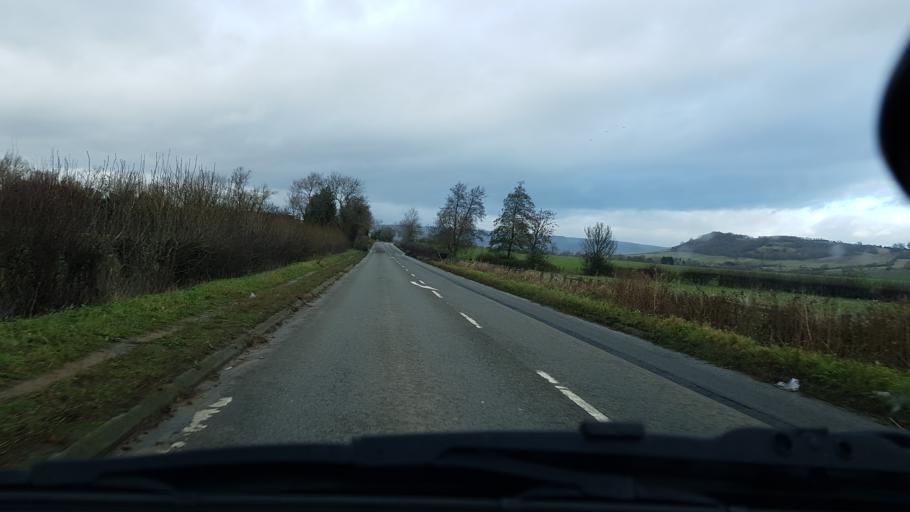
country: GB
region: England
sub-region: Gloucestershire
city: Gotherington
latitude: 51.9671
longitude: -2.0703
